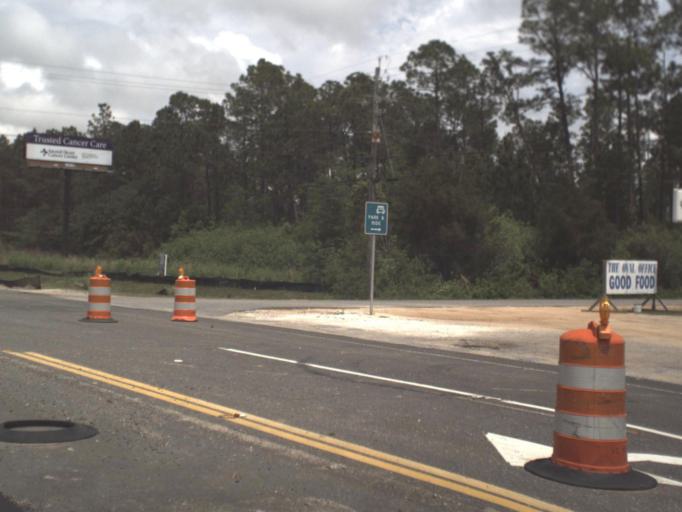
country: US
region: Florida
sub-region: Santa Rosa County
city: Bagdad
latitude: 30.5368
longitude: -87.0872
